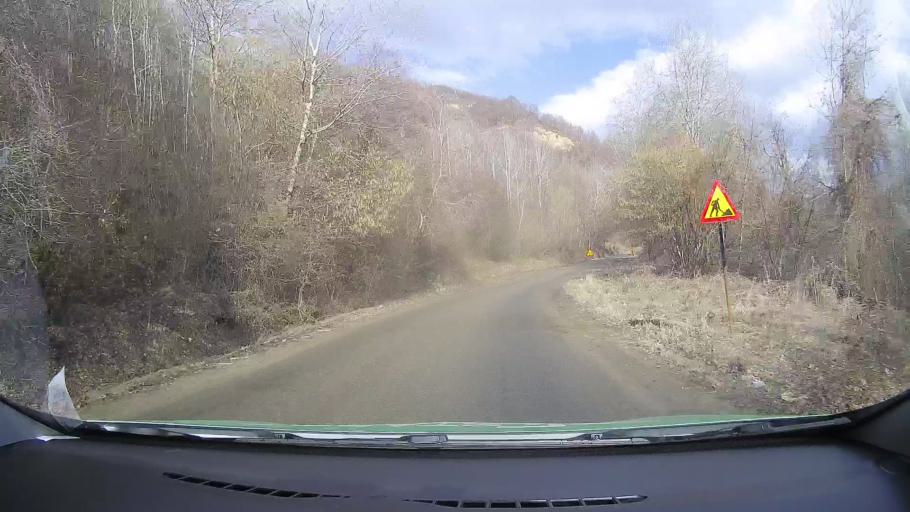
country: RO
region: Dambovita
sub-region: Comuna Motaeni
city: Motaeni
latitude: 45.1015
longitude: 25.4406
